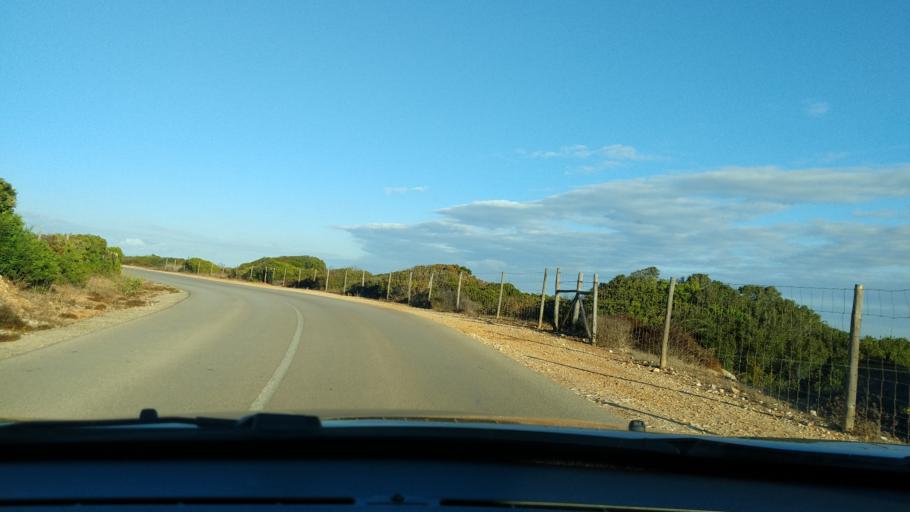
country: PT
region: Faro
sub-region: Vila do Bispo
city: Sagres
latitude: 37.0211
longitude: -8.9355
